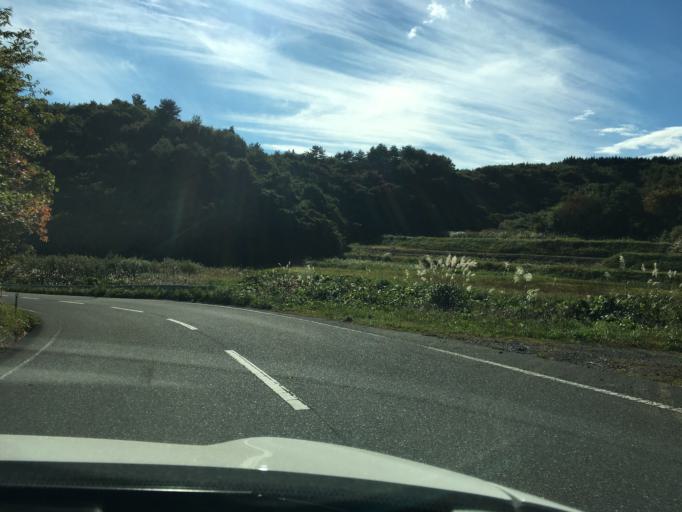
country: JP
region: Fukushima
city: Ishikawa
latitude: 37.1542
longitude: 140.5963
